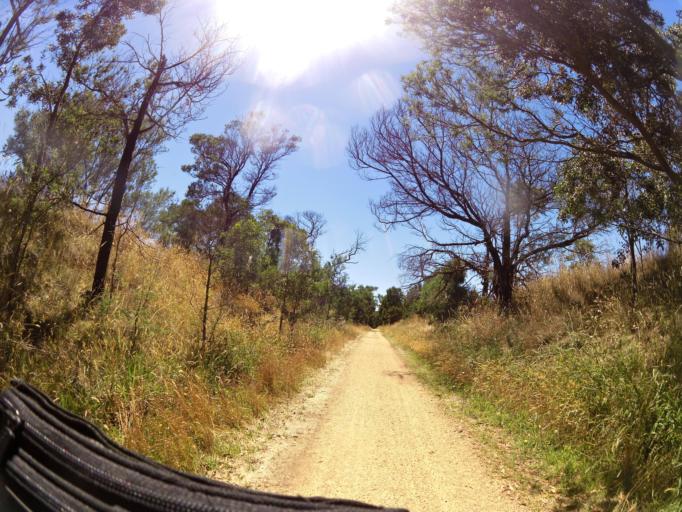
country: AU
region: Victoria
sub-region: Ballarat North
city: Delacombe
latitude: -37.7021
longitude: 143.6477
